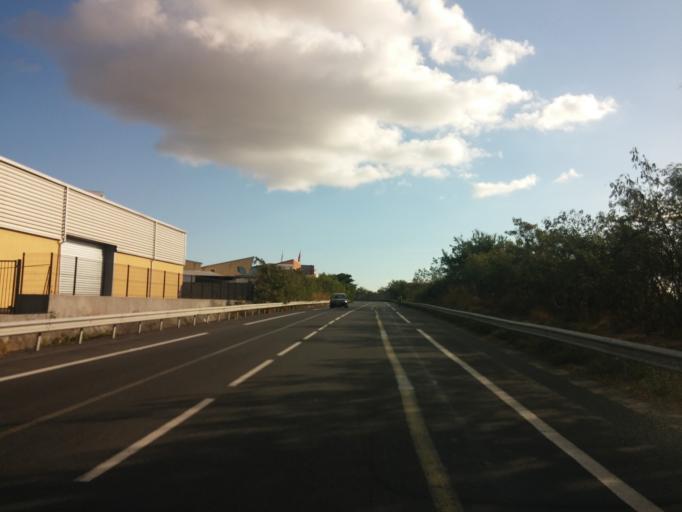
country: RE
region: Reunion
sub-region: Reunion
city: La Possession
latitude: -20.9355
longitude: 55.3278
